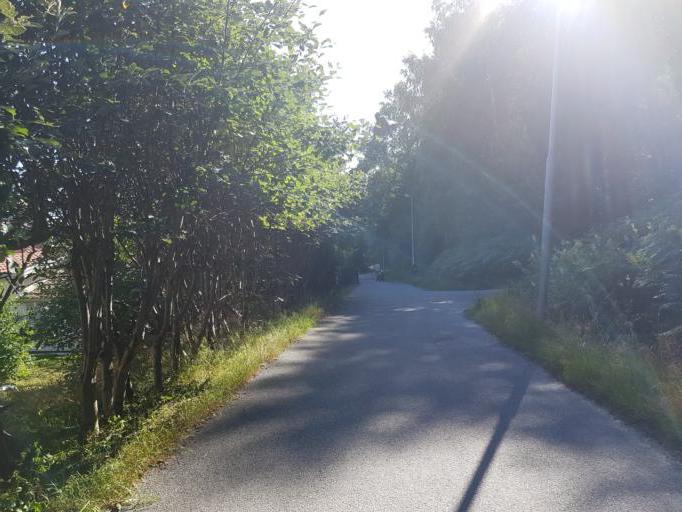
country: SE
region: Vaestra Goetaland
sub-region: Partille Kommun
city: Furulund
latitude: 57.7042
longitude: 12.1452
